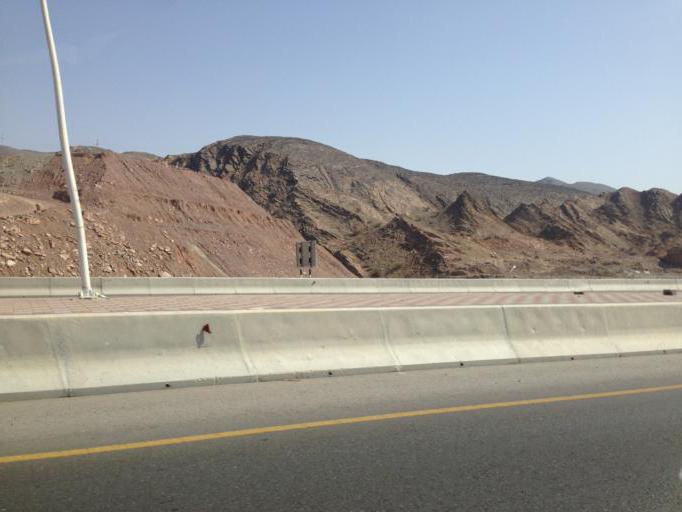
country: OM
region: Muhafazat Masqat
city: Bawshar
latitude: 23.5923
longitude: 58.4679
